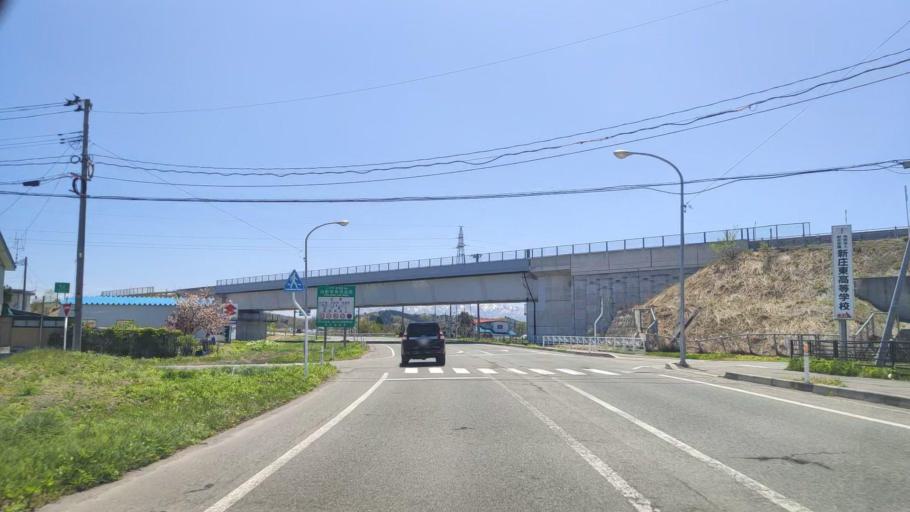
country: JP
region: Yamagata
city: Shinjo
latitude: 38.7454
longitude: 140.2949
